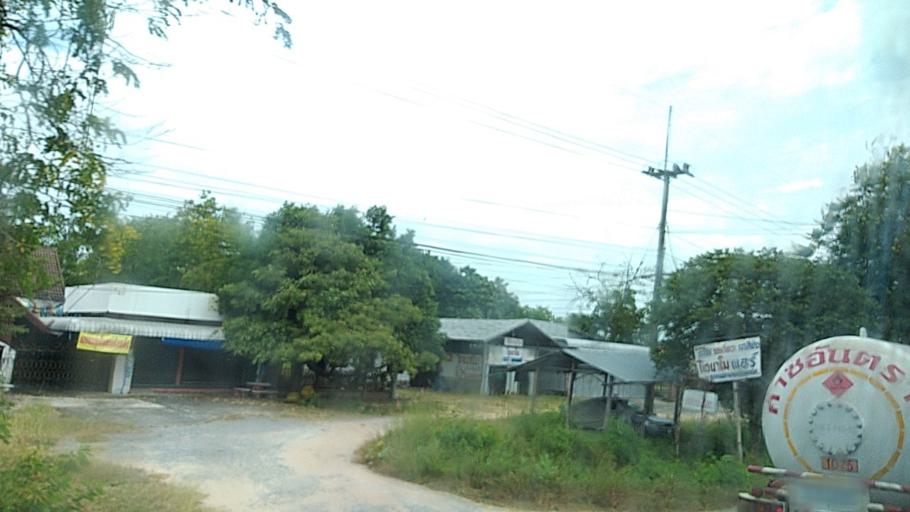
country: TH
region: Roi Et
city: Changhan
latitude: 16.1104
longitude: 103.5068
